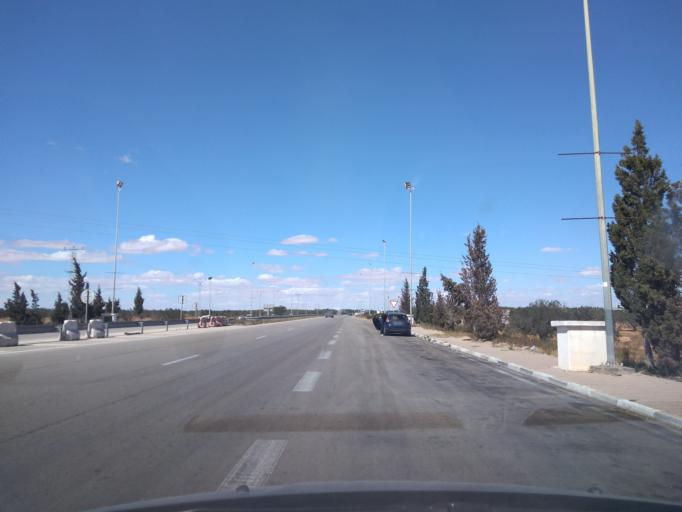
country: TN
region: Safaqis
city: Al Qarmadah
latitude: 34.8857
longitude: 10.7227
